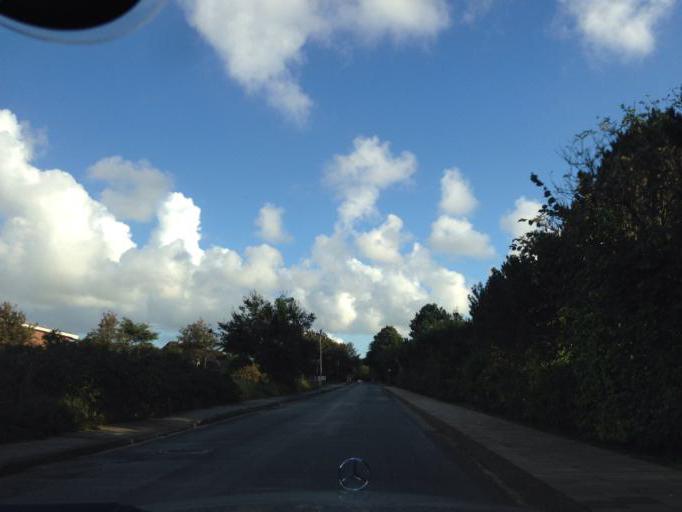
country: DE
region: Schleswig-Holstein
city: Wyk auf Fohr
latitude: 54.6926
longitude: 8.5581
